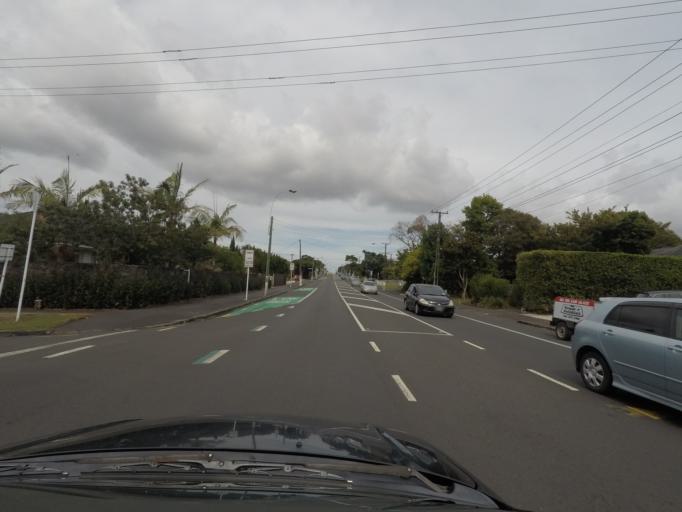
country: NZ
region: Auckland
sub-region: Auckland
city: Auckland
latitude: -36.8810
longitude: 174.7398
